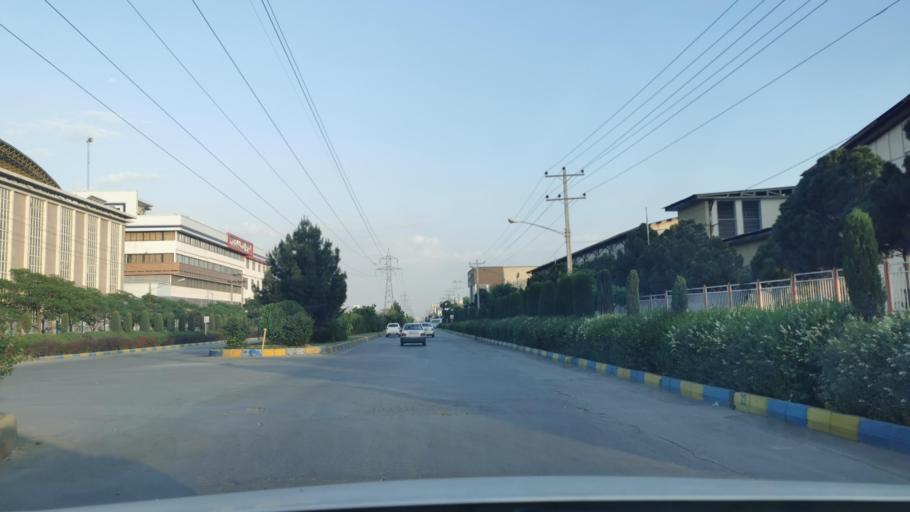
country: IR
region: Razavi Khorasan
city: Torqabeh
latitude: 36.4280
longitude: 59.4202
